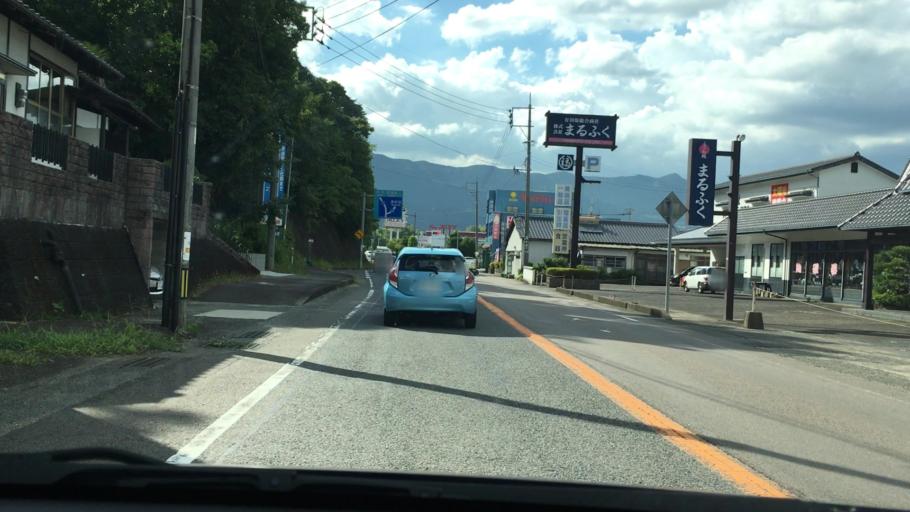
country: JP
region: Saga Prefecture
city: Imaricho-ko
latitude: 33.1884
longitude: 129.8640
